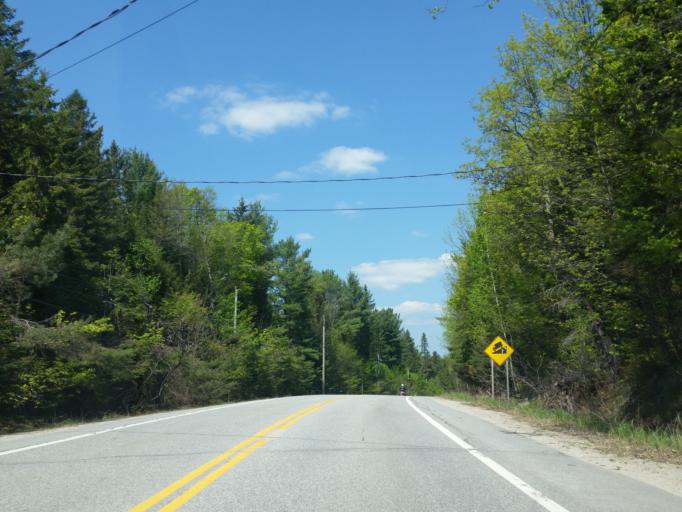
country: CA
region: Quebec
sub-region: Outaouais
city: Wakefield
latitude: 45.5767
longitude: -75.8746
